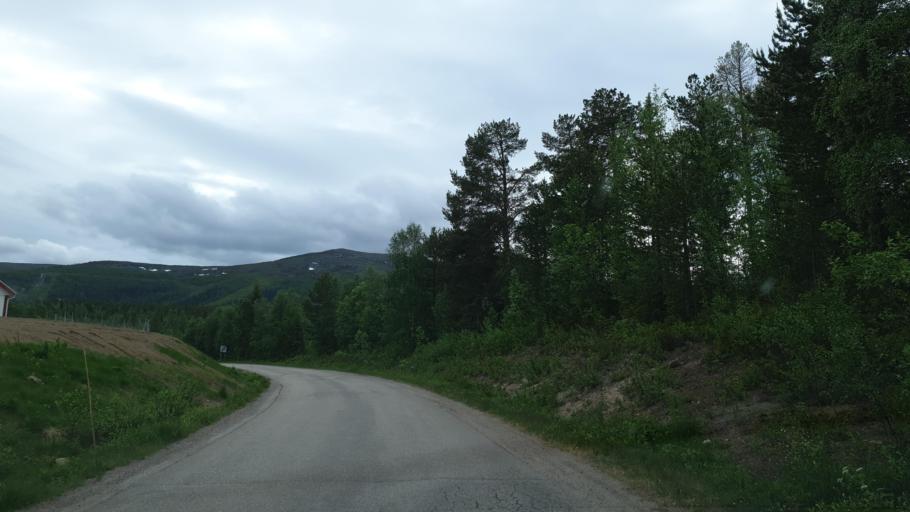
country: SE
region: Norrbotten
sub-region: Gallivare Kommun
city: Gaellivare
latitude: 67.1315
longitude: 20.6277
